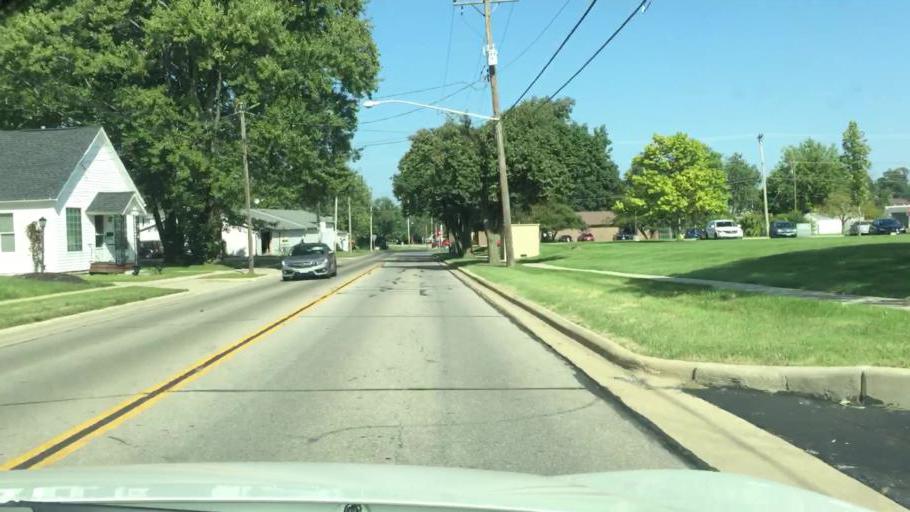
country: US
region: Ohio
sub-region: Union County
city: Marysville
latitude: 40.2305
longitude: -83.3746
